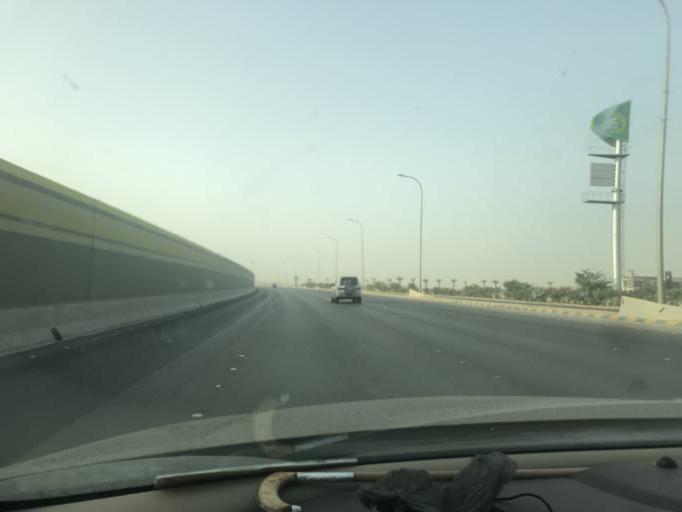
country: SA
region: Ar Riyad
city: Riyadh
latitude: 24.8913
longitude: 46.6953
